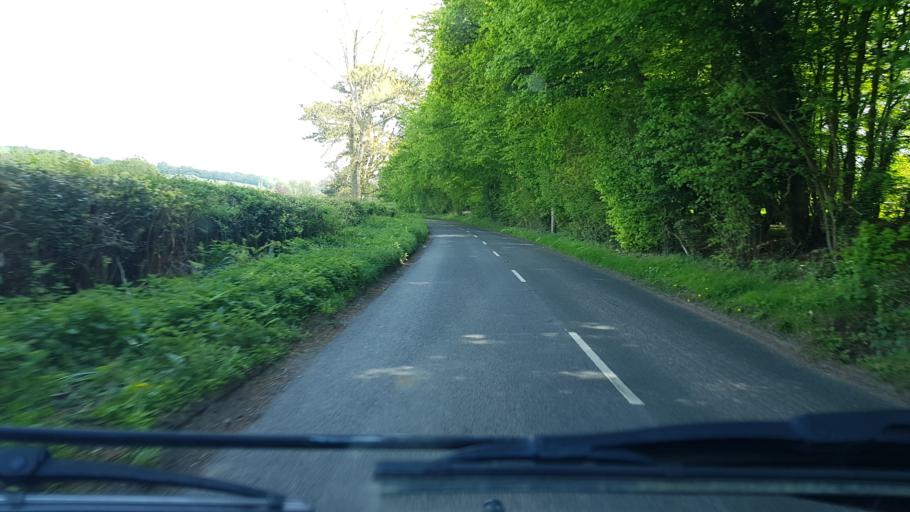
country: GB
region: England
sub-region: East Sussex
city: Robertsbridge
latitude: 51.0340
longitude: 0.4382
